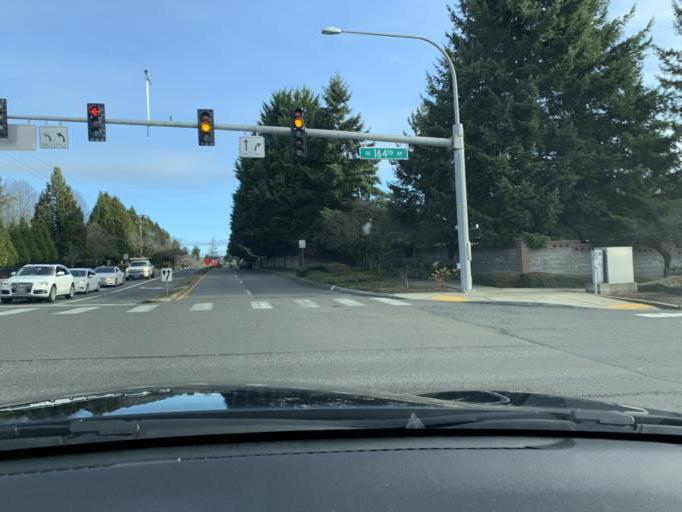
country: US
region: Washington
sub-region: Clark County
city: Mill Plain
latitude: 45.5967
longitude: -122.5039
